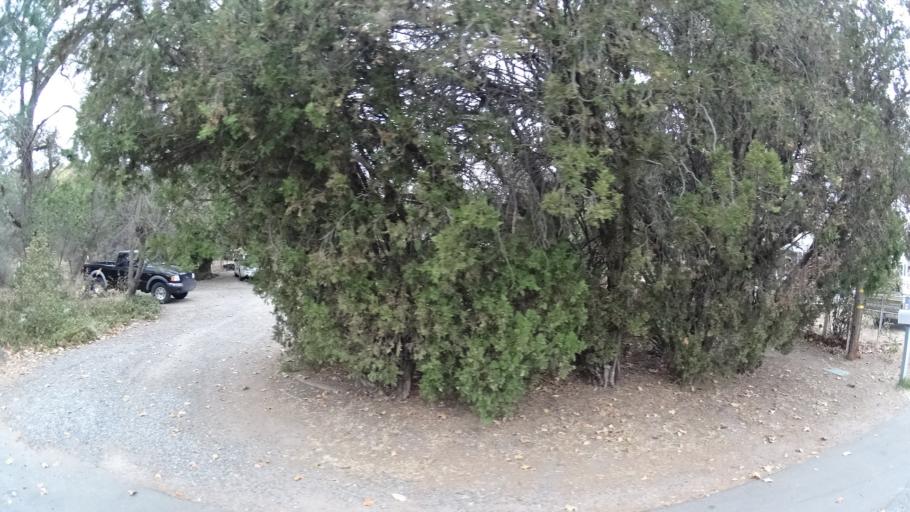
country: US
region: California
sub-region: Sacramento County
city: Citrus Heights
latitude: 38.7039
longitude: -121.2988
